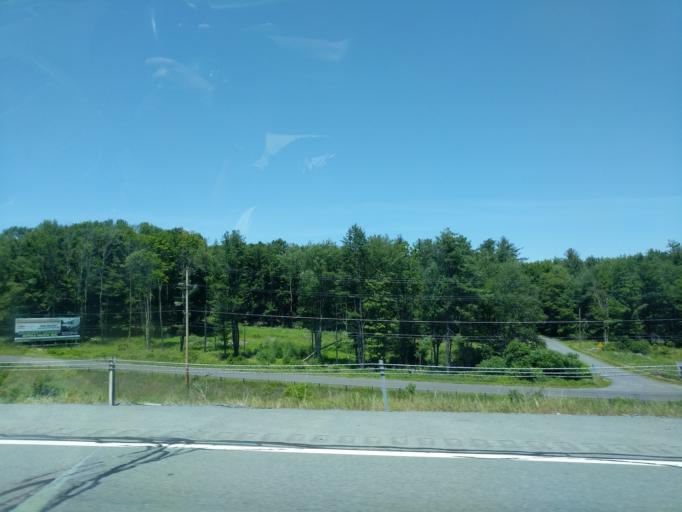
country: US
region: New York
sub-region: Sullivan County
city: Rock Hill
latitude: 41.6401
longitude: -74.6351
